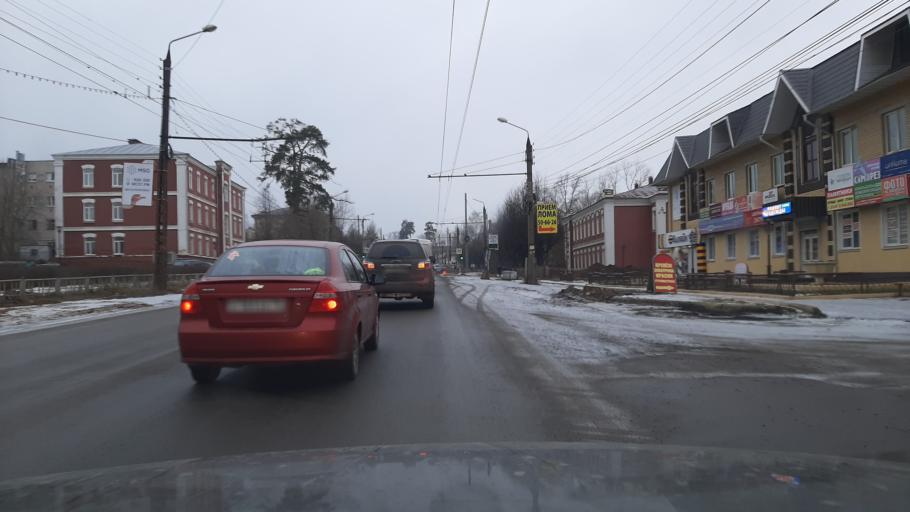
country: RU
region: Ivanovo
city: Kokhma
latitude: 56.9321
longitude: 41.0784
